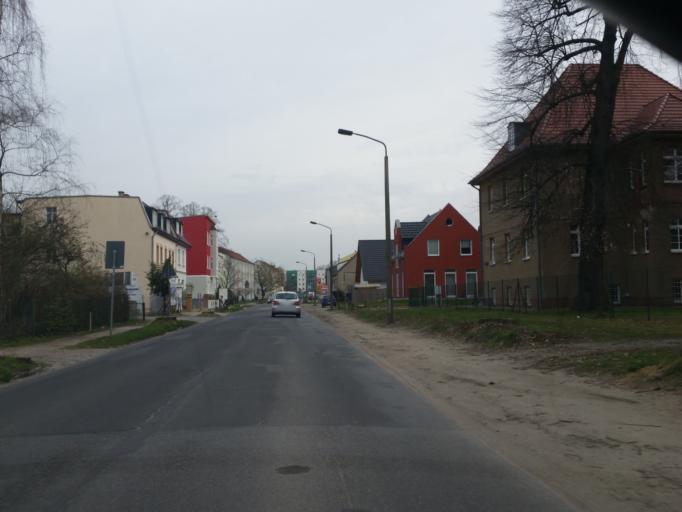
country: DE
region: Brandenburg
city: Teltow
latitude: 52.3971
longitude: 13.2677
